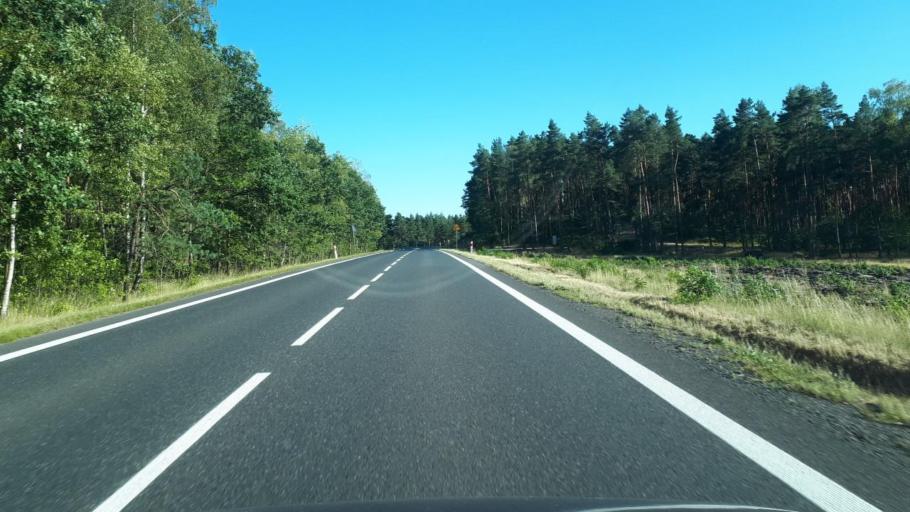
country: PL
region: Silesian Voivodeship
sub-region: Powiat lubliniecki
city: Lubliniec
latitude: 50.6007
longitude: 18.7015
